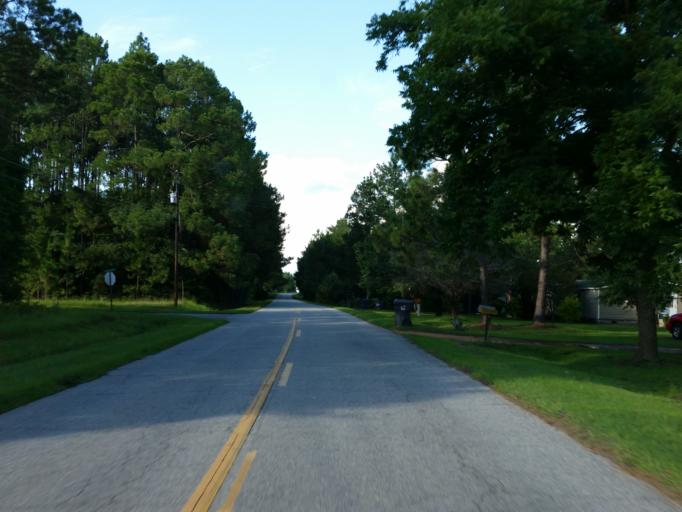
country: US
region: Georgia
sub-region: Dooly County
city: Vienna
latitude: 32.0804
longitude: -83.8045
